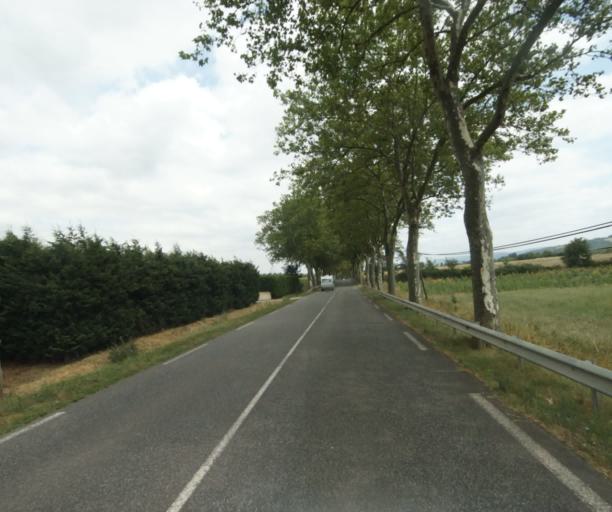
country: FR
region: Midi-Pyrenees
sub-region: Departement de la Haute-Garonne
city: Revel
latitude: 43.4495
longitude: 1.9706
